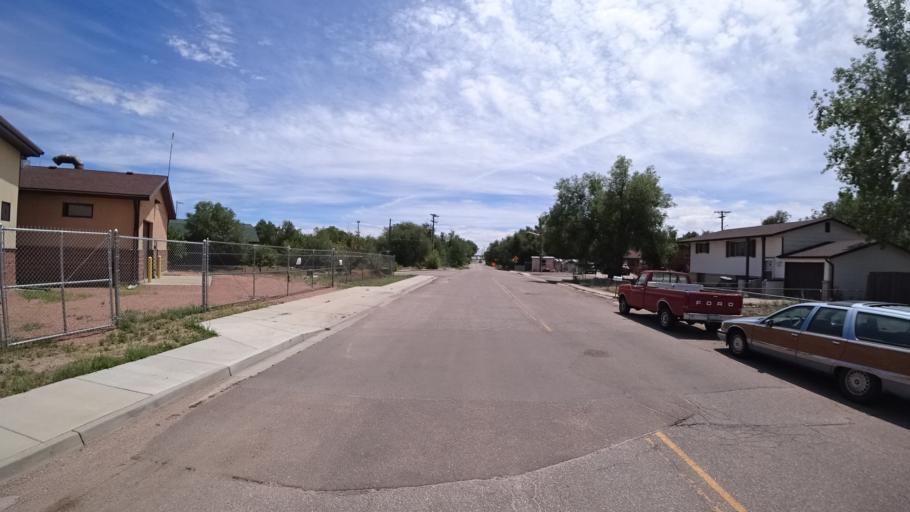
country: US
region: Colorado
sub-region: El Paso County
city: Security-Widefield
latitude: 38.7277
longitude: -104.7272
